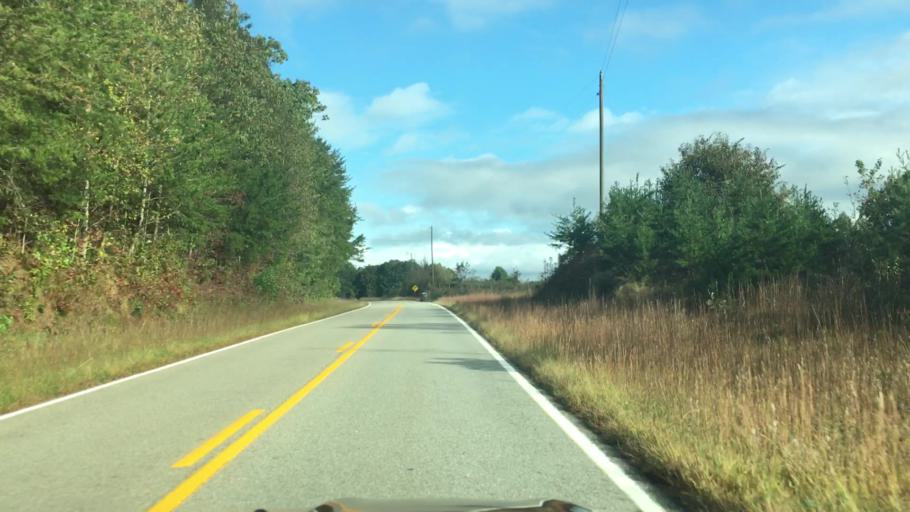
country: US
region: Georgia
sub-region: Lumpkin County
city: Dahlonega
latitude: 34.6015
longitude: -83.8959
